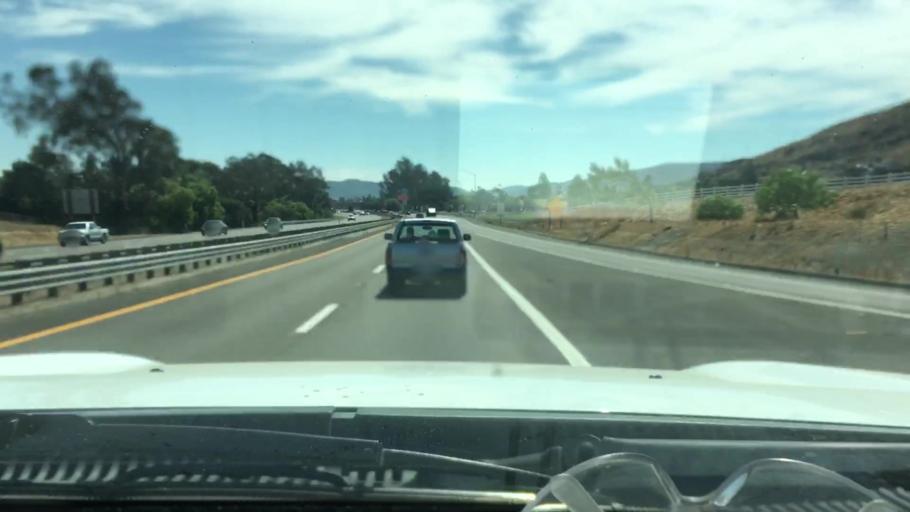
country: US
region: California
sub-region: San Luis Obispo County
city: San Luis Obispo
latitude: 35.2719
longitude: -120.6725
